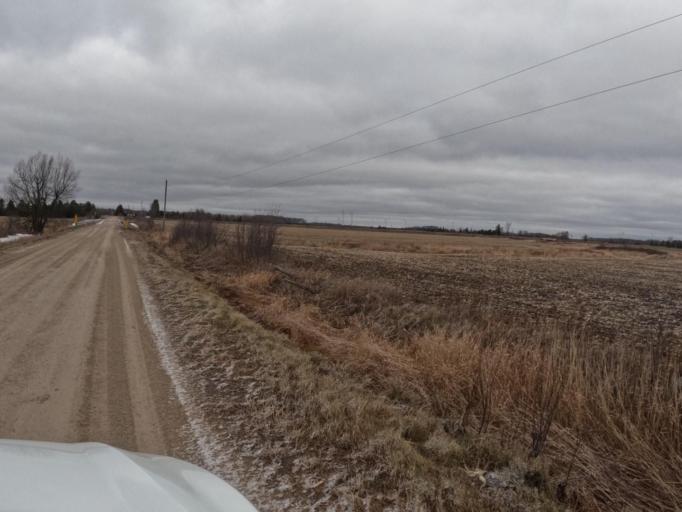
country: CA
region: Ontario
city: Shelburne
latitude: 44.0361
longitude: -80.3724
